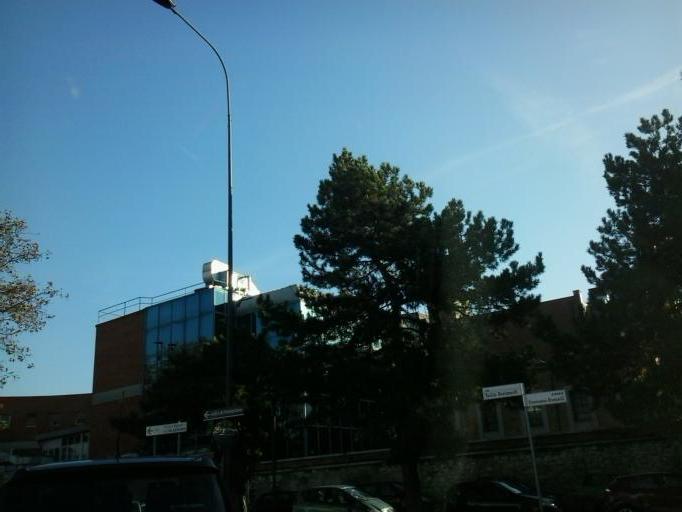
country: IT
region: Lombardy
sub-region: Provincia di Brescia
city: Brescia
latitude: 45.5579
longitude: 10.2279
